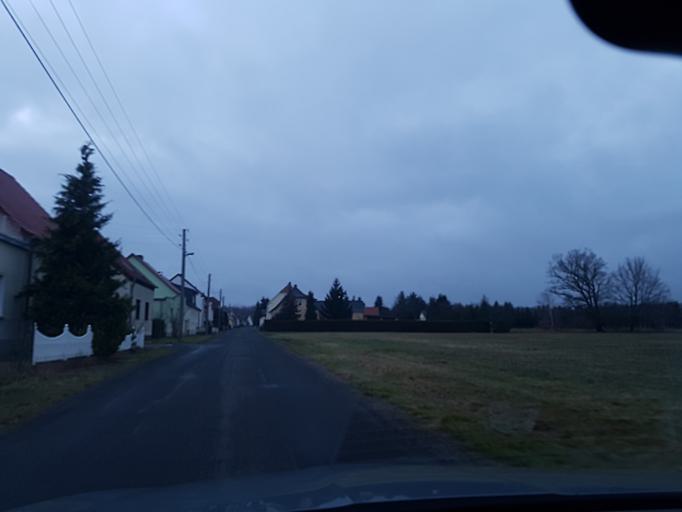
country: DE
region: Brandenburg
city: Schonborn
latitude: 51.5966
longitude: 13.4920
